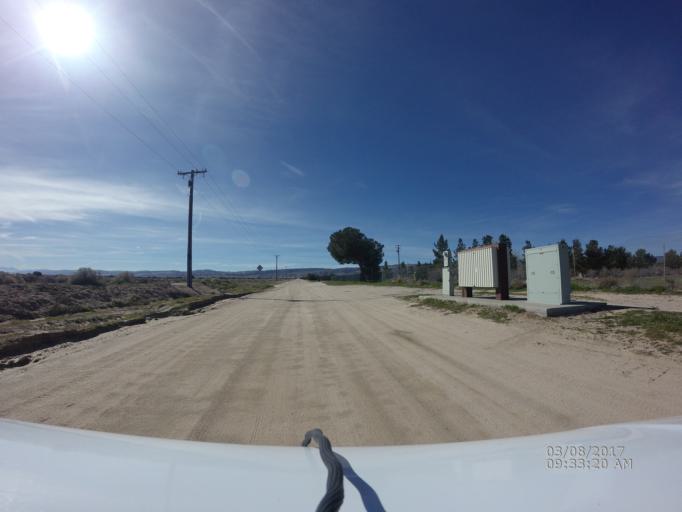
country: US
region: California
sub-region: Los Angeles County
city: Green Valley
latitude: 34.7737
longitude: -118.4667
